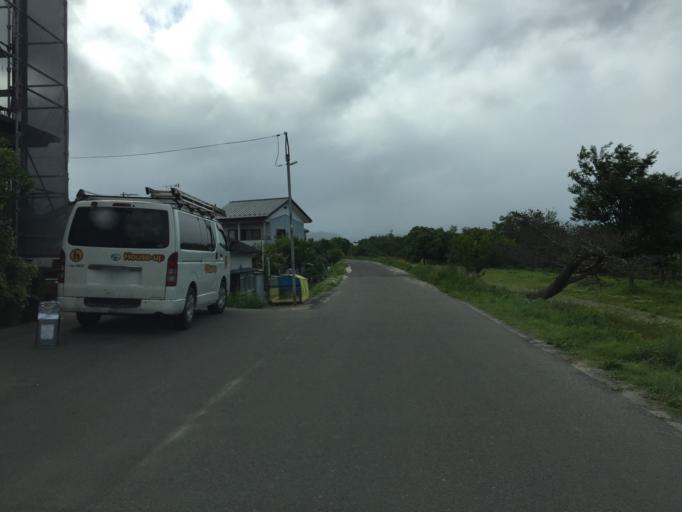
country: JP
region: Fukushima
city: Fukushima-shi
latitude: 37.7802
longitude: 140.4810
